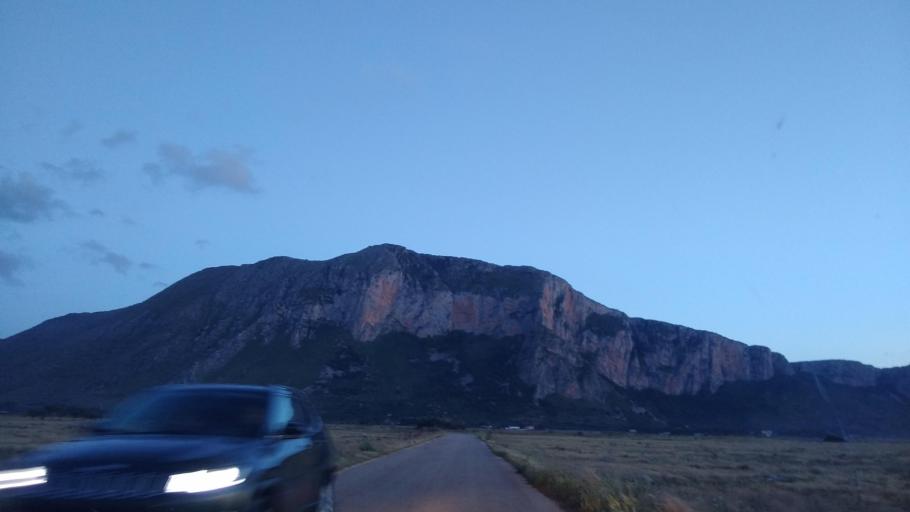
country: IT
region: Sicily
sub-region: Trapani
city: Castelluzzo
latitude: 38.1160
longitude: 12.7206
